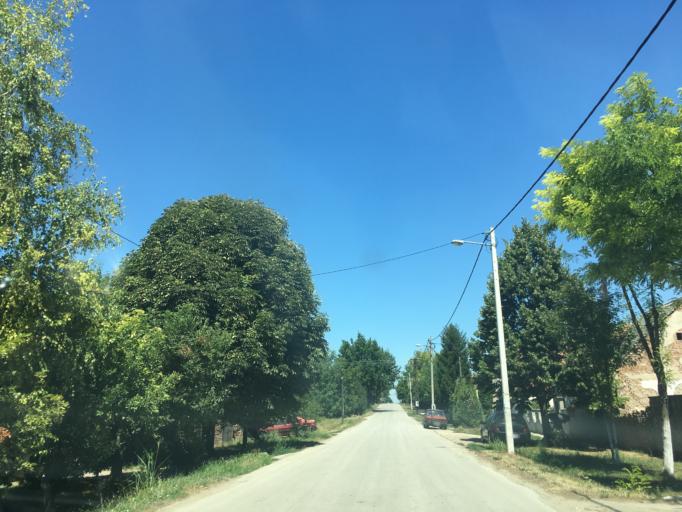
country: RS
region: Central Serbia
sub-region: Belgrade
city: Grocka
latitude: 44.7301
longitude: 20.8205
